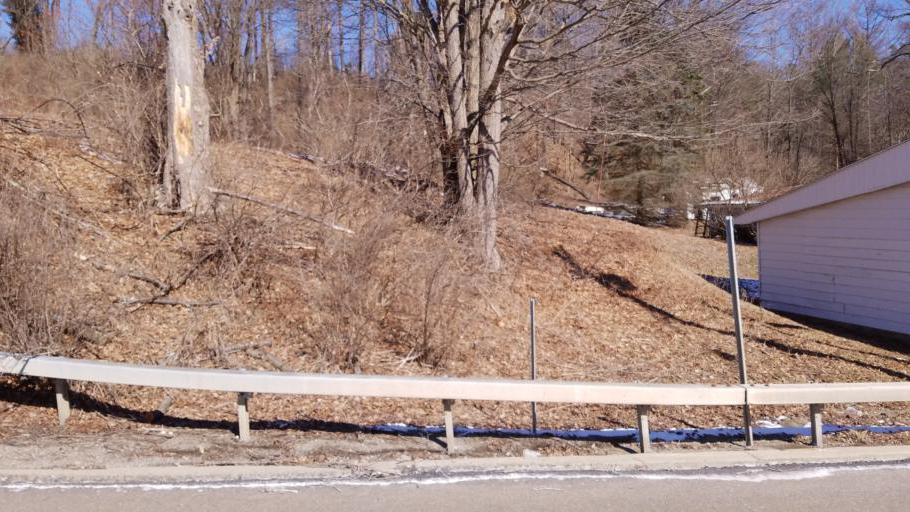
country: US
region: New York
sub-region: Allegany County
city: Andover
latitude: 42.0381
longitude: -77.7834
